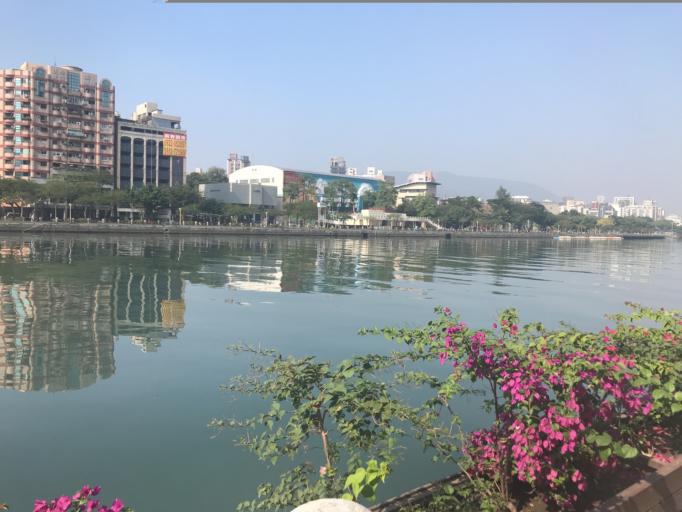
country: TW
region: Kaohsiung
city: Kaohsiung
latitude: 22.6218
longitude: 120.2907
